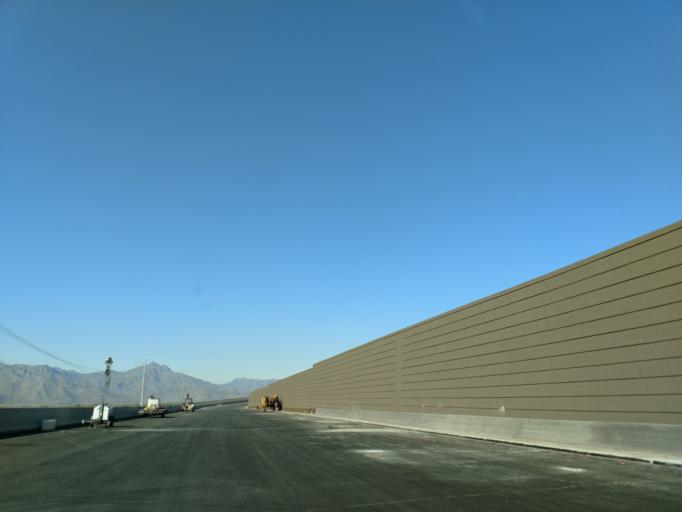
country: US
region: Arizona
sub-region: Maricopa County
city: Laveen
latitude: 33.2912
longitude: -112.1245
